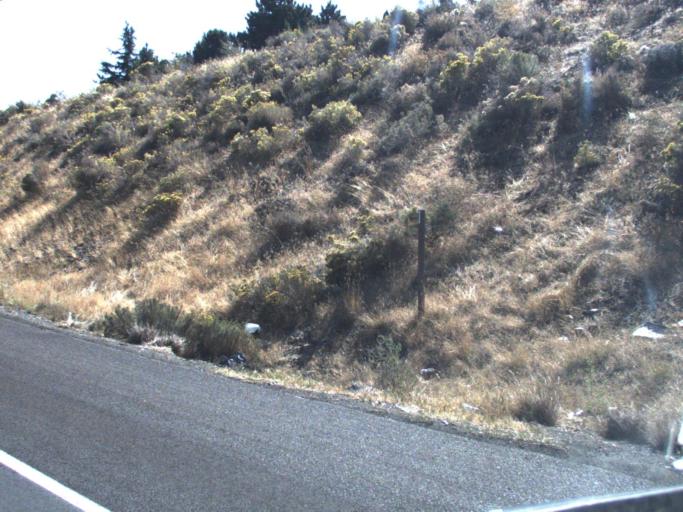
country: US
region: Washington
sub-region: Franklin County
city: West Pasco
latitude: 46.2285
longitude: -119.1905
